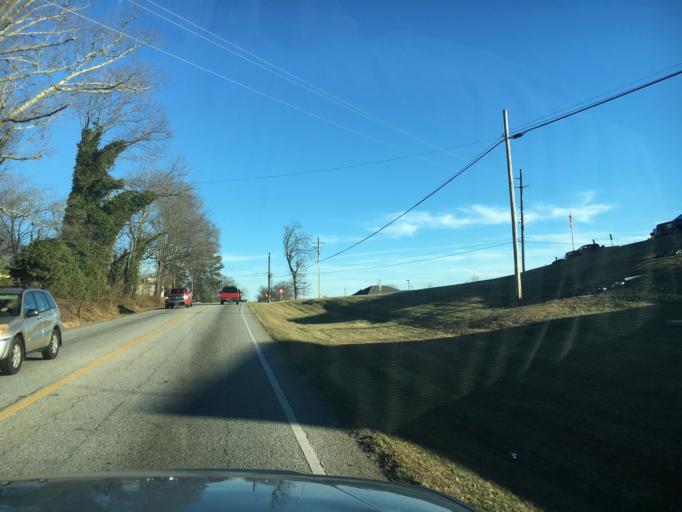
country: US
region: Georgia
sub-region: Habersham County
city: Demorest
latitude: 34.5464
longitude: -83.5498
